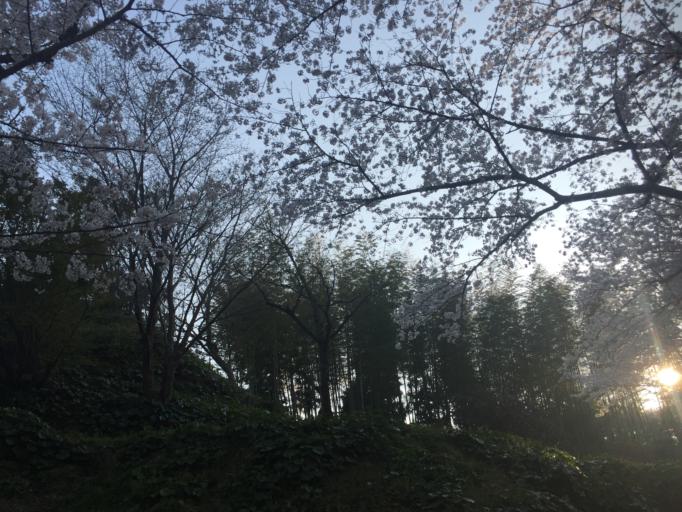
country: JP
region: Shizuoka
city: Kosai-shi
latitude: 34.7620
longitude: 137.6327
